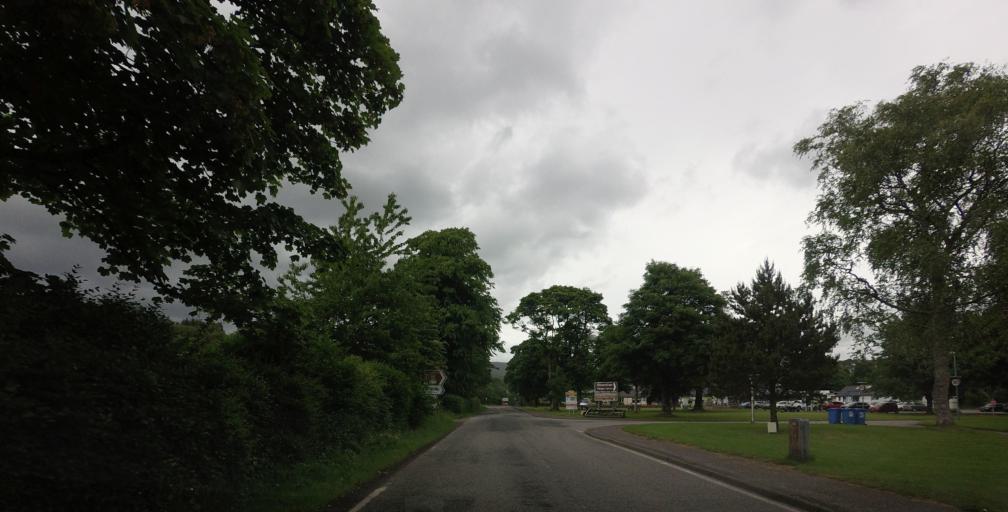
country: GB
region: Scotland
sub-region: Argyll and Bute
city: Oban
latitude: 56.6945
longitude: -5.5707
